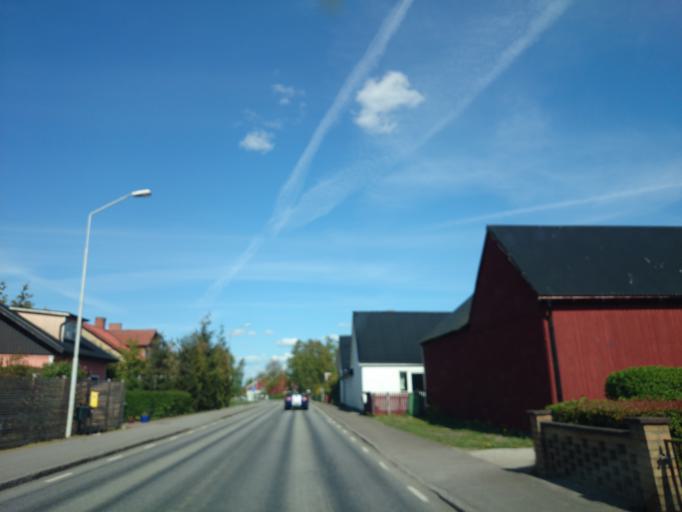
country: SE
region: Skane
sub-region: Kavlinge Kommun
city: Loddekopinge
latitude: 55.7669
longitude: 13.0506
